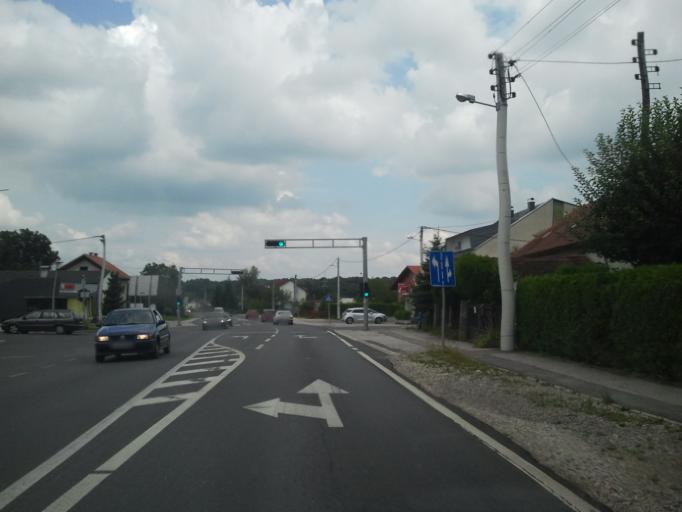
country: HR
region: Zagrebacka
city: Kerestinec
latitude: 45.7383
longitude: 15.7968
